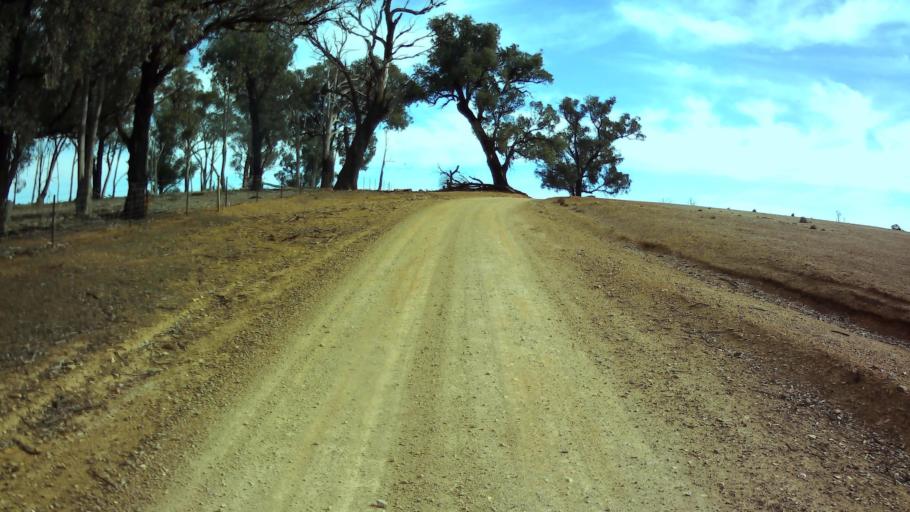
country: AU
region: New South Wales
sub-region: Weddin
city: Grenfell
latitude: -33.8944
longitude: 148.2042
